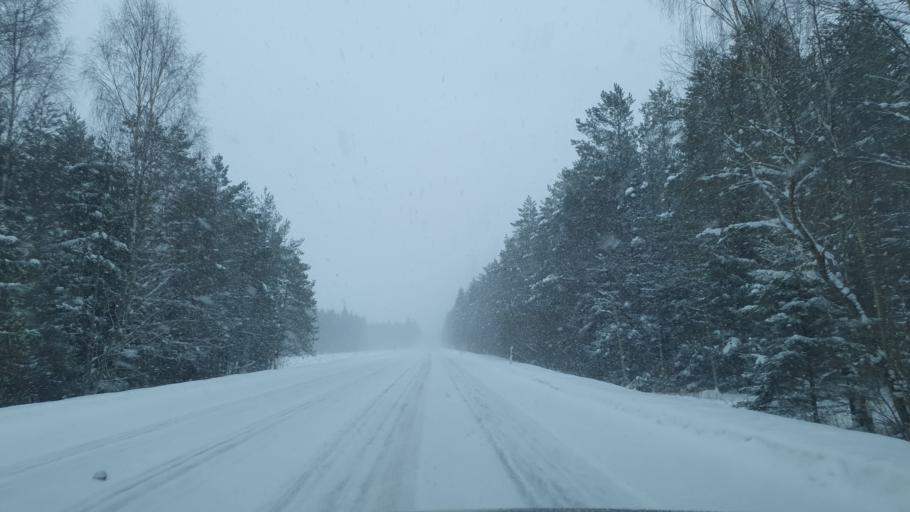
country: EE
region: Laeaene-Virumaa
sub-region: Rakke vald
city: Rakke
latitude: 58.9329
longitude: 26.2196
